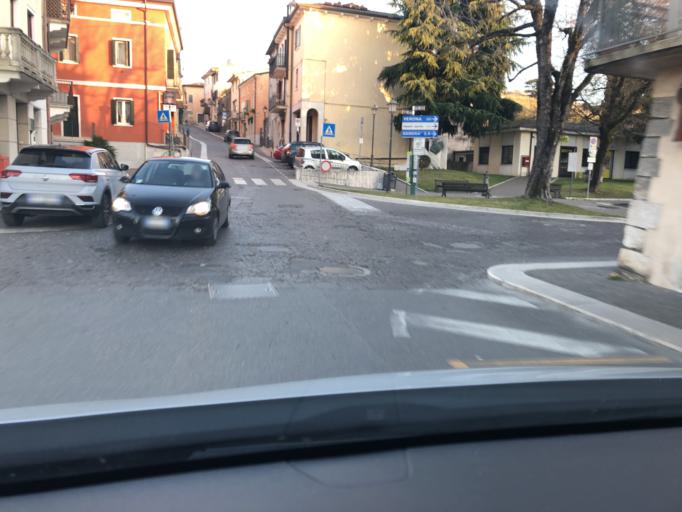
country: IT
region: Veneto
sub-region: Provincia di Verona
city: Sona
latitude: 45.4530
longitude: 10.8178
